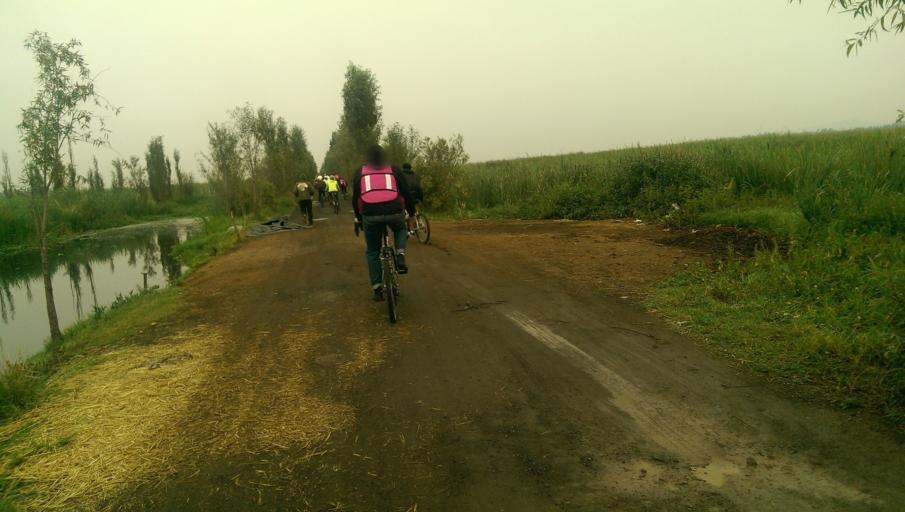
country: MX
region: Mexico City
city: Tlahuac
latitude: 19.2651
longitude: -99.0512
